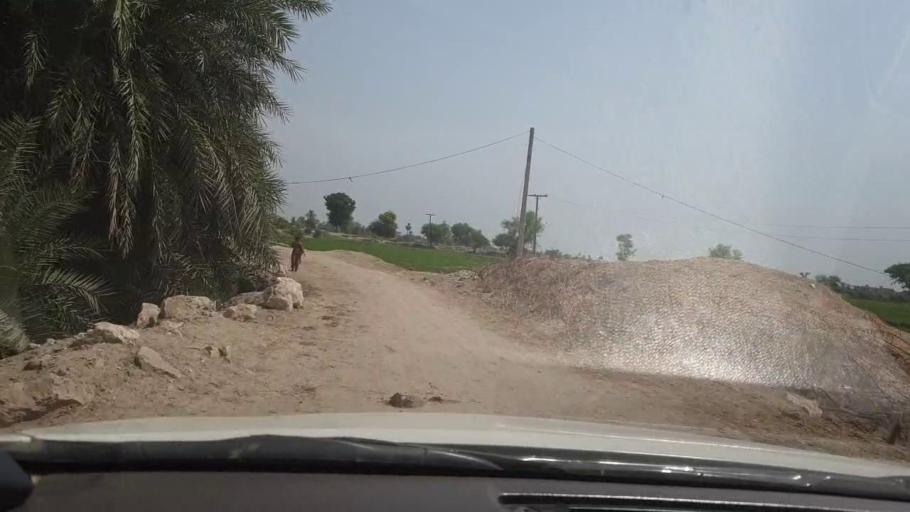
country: PK
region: Sindh
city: Shikarpur
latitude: 27.9423
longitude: 68.5978
